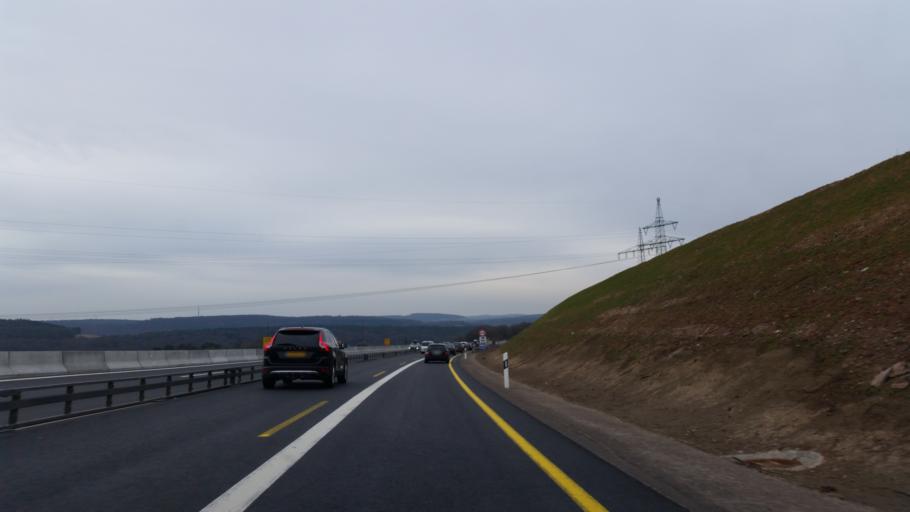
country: DE
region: Bavaria
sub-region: Regierungsbezirk Unterfranken
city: Marktheidenfeld
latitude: 49.7979
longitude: 9.5871
